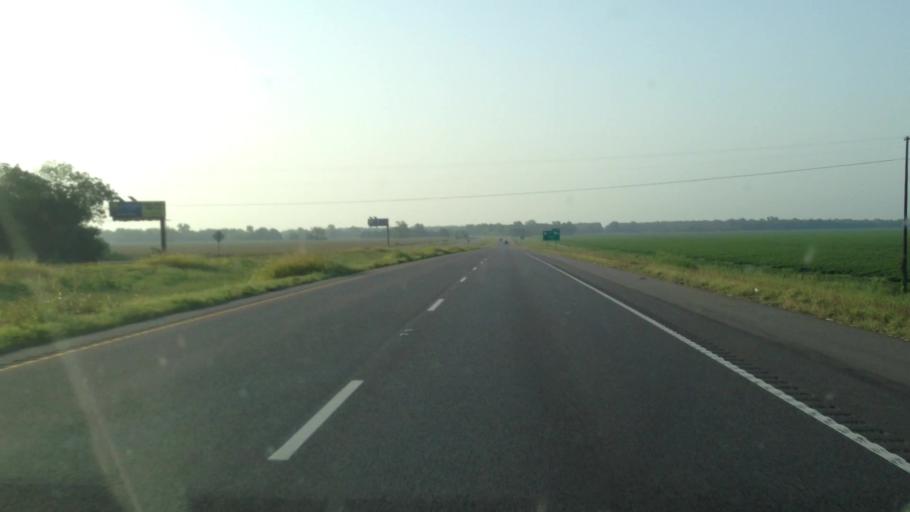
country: US
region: Louisiana
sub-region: Rapides Parish
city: Boyce
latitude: 31.3912
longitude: -92.6913
